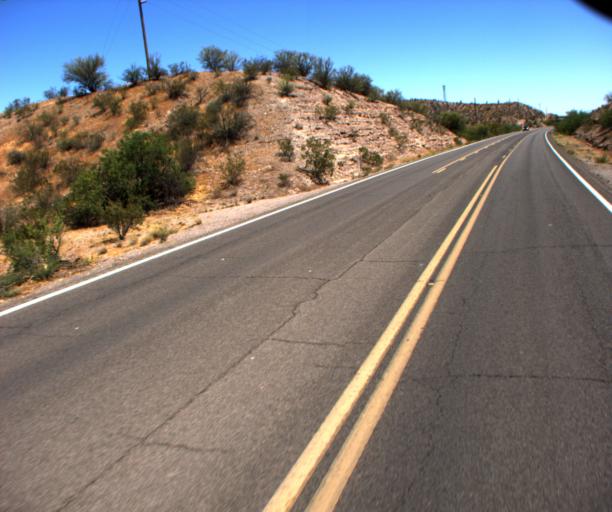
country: US
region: Arizona
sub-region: Pinal County
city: Kearny
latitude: 32.9506
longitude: -110.7439
